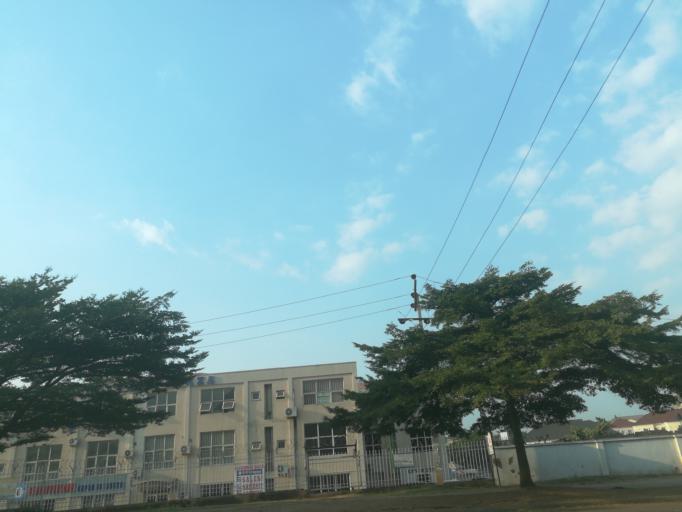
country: NG
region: Abuja Federal Capital Territory
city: Abuja
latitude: 9.0658
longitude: 7.4318
